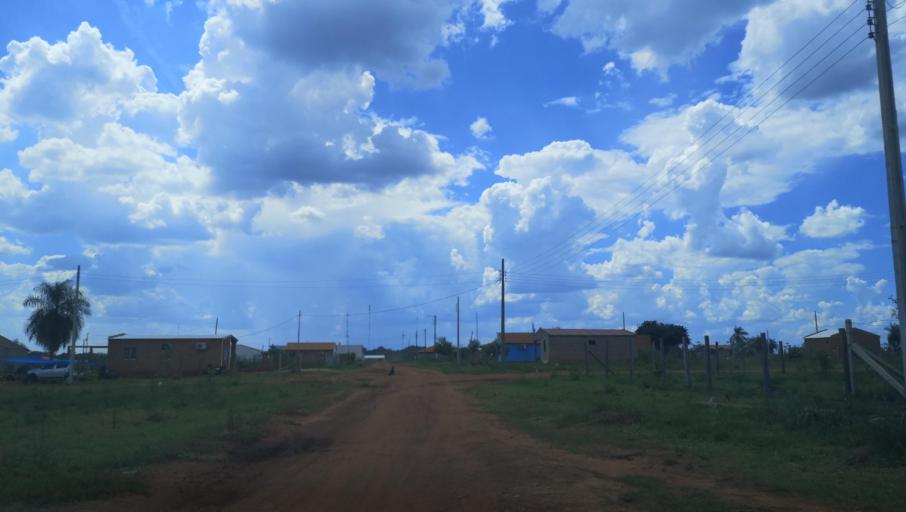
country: PY
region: Misiones
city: Santa Maria
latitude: -26.8983
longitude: -57.0406
